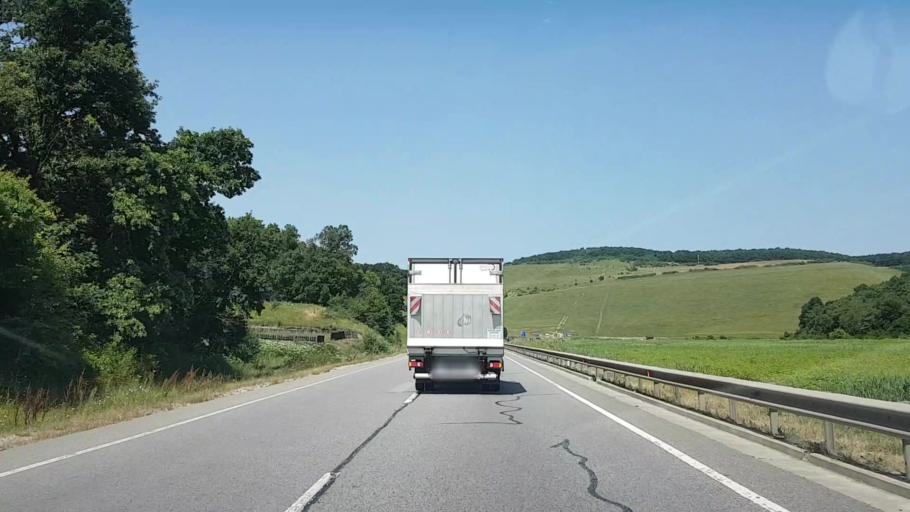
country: RO
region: Cluj
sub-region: Comuna Apahida
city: Dezmir
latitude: 46.7384
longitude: 23.7081
